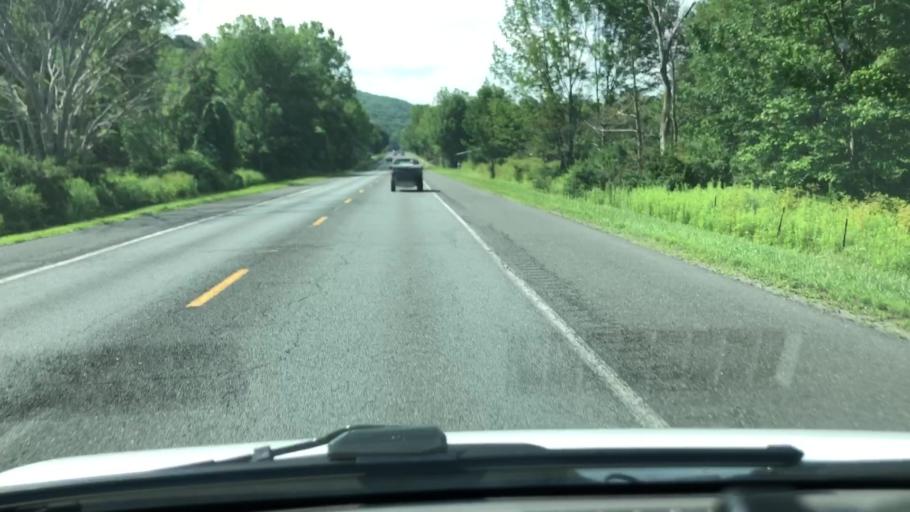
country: US
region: Massachusetts
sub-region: Berkshire County
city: Lanesborough
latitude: 42.5197
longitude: -73.1924
